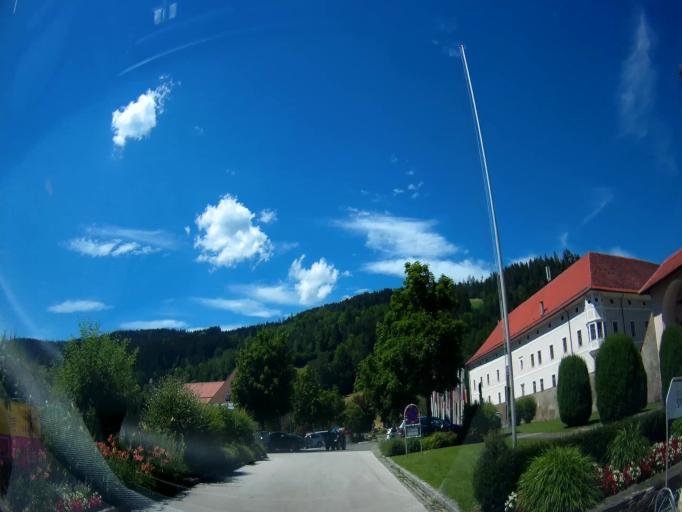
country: AT
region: Carinthia
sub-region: Politischer Bezirk Sankt Veit an der Glan
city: Gurk
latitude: 46.8747
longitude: 14.2920
